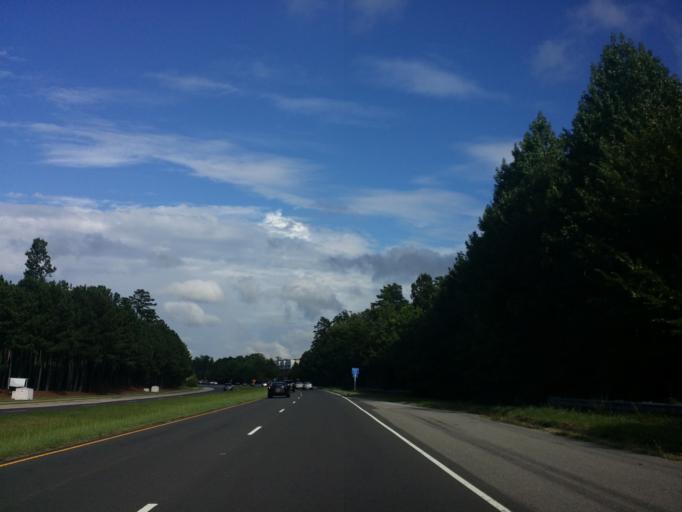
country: US
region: North Carolina
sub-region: Wake County
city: Morrisville
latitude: 35.9178
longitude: -78.7955
